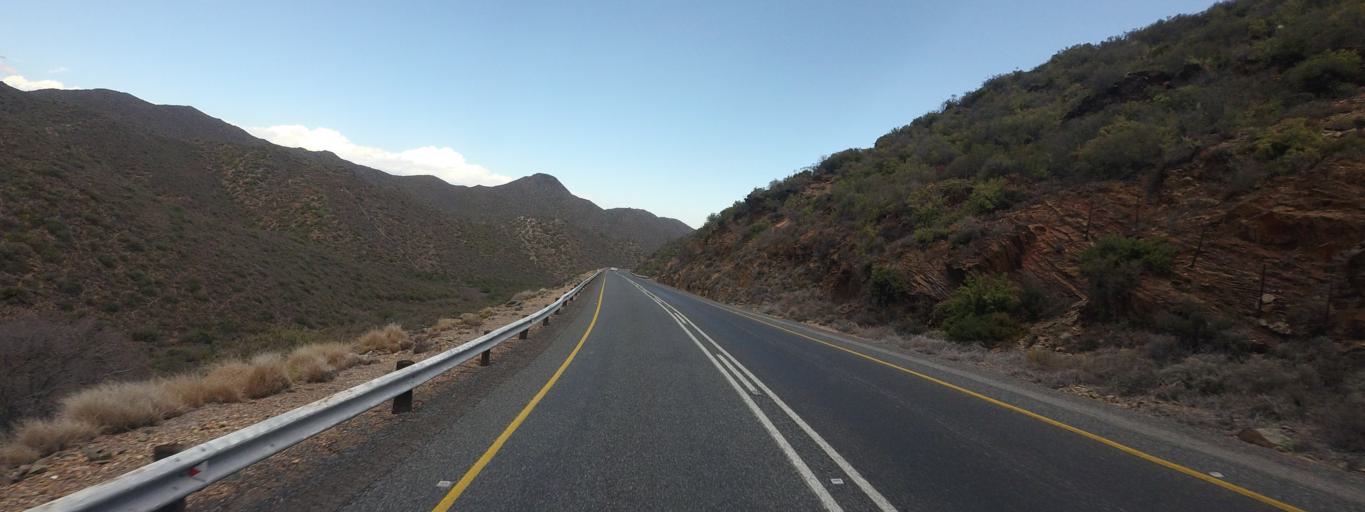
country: ZA
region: Western Cape
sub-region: Eden District Municipality
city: Ladismith
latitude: -33.4760
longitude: 21.5572
